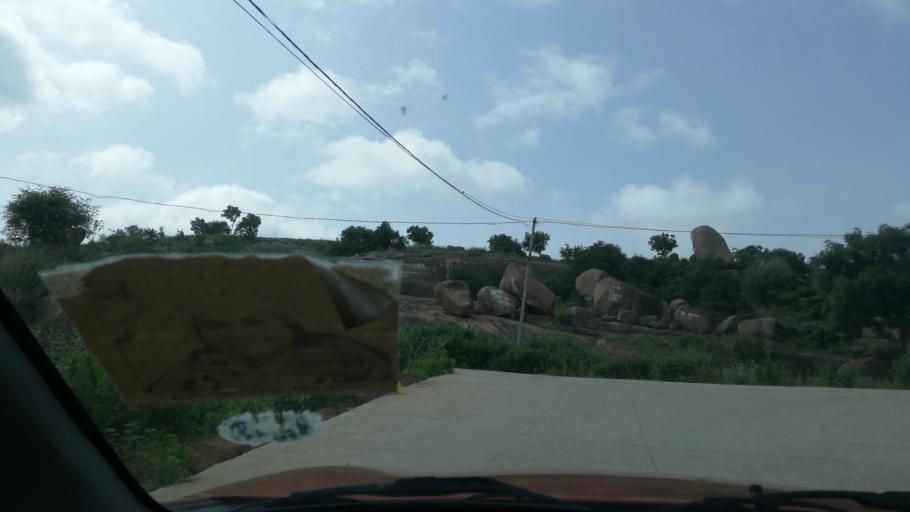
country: IN
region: Telangana
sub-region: Rangareddi
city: Kukatpalli
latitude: 17.4122
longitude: 78.3660
